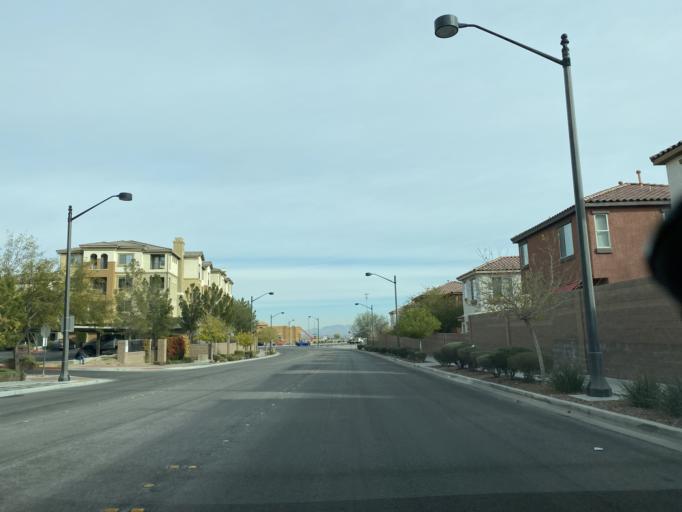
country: US
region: Nevada
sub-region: Clark County
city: Summerlin South
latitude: 36.2955
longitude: -115.2914
